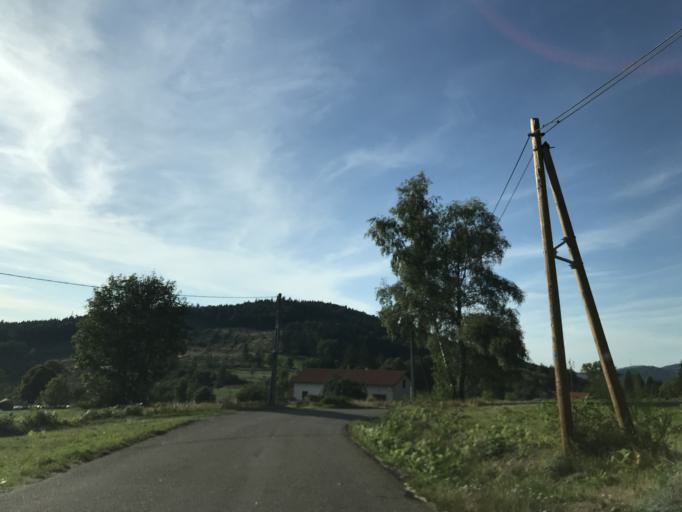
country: FR
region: Auvergne
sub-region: Departement du Puy-de-Dome
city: Job
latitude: 45.6786
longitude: 3.7301
